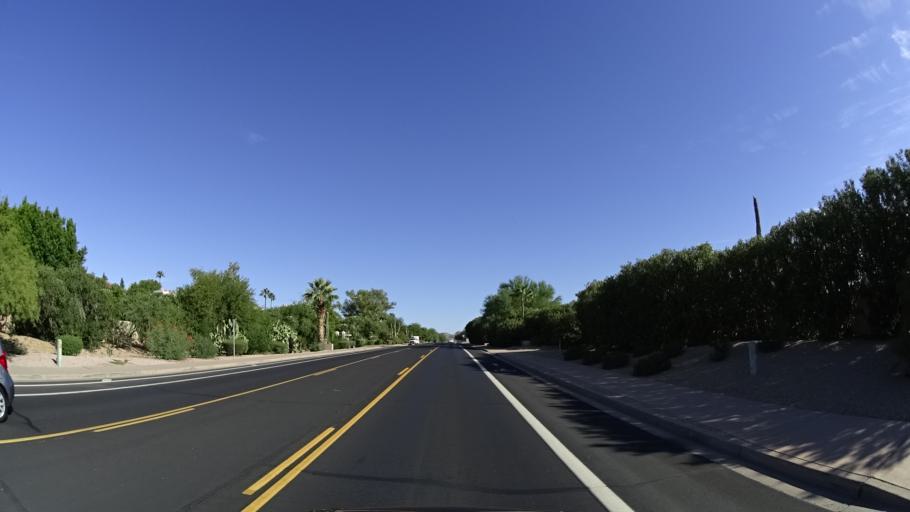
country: US
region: Arizona
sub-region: Maricopa County
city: Paradise Valley
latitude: 33.5114
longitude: -111.9433
